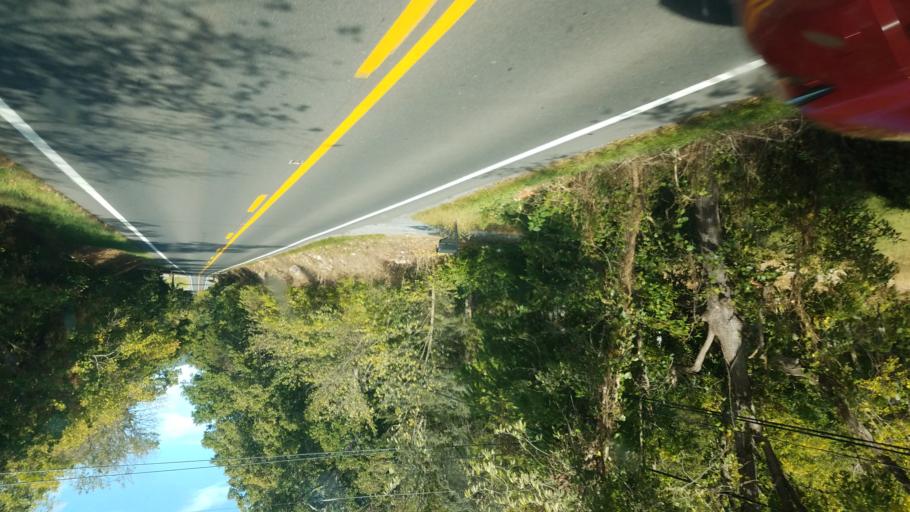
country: US
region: Virginia
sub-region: Warren County
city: Front Royal
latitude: 38.8599
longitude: -78.2653
